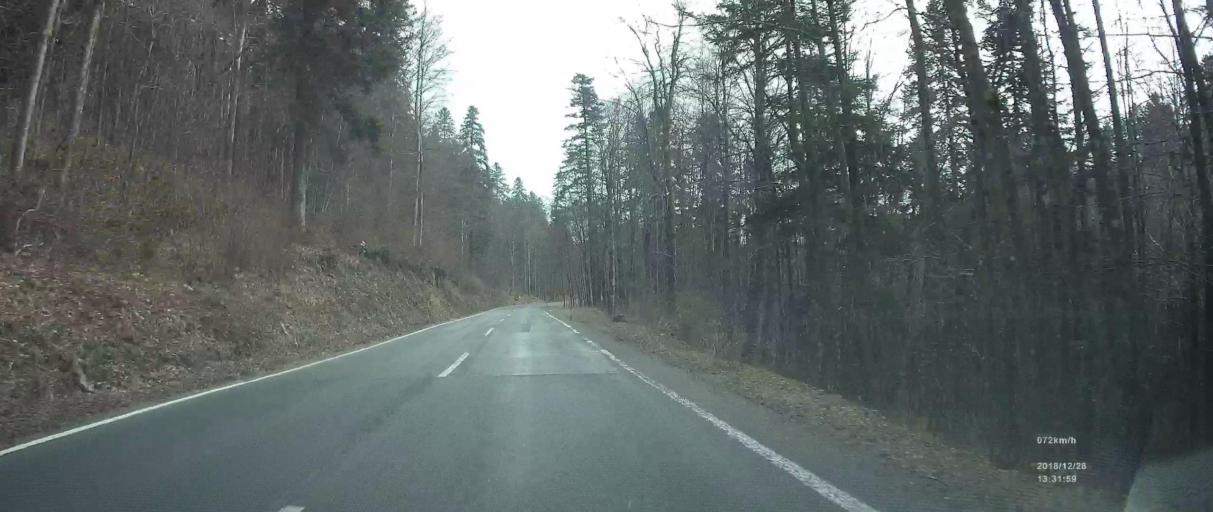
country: HR
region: Primorsko-Goranska
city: Hreljin
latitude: 45.3495
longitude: 14.6589
